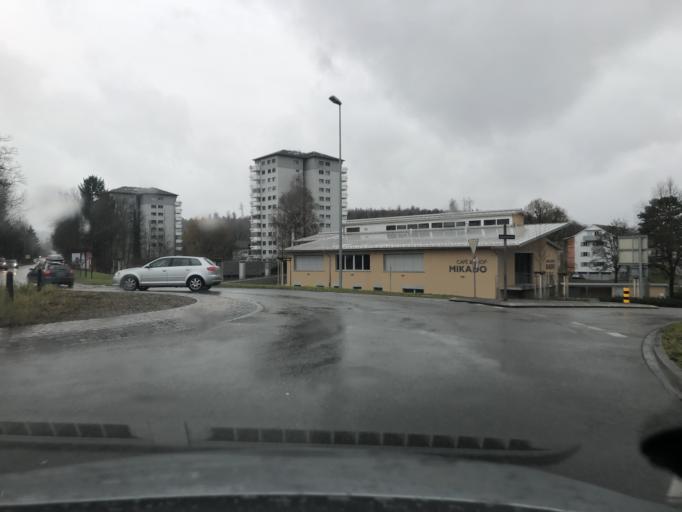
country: CH
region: Aargau
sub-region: Bezirk Brugg
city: Windisch
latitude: 47.4745
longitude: 8.2128
